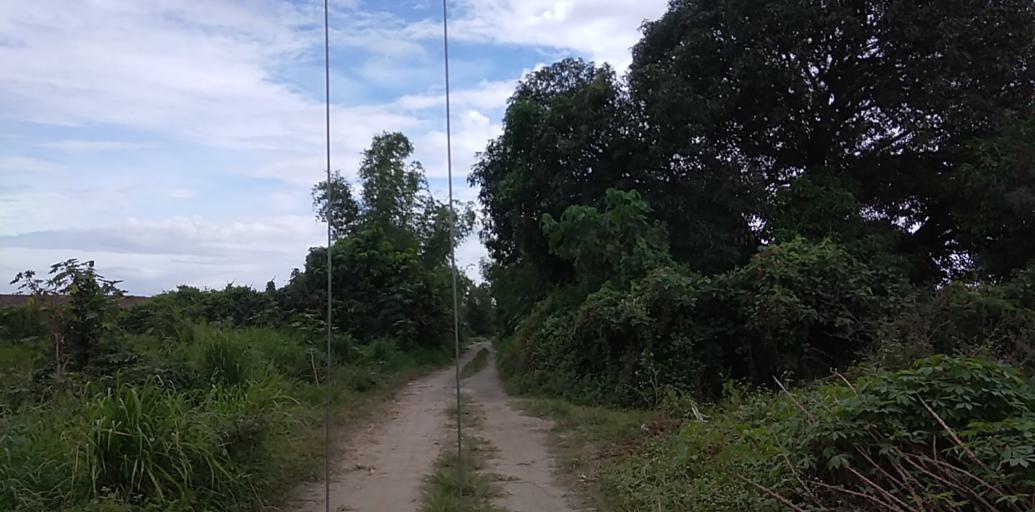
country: PH
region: Central Luzon
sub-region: Province of Pampanga
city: Pulung Santol
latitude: 15.0361
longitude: 120.5610
